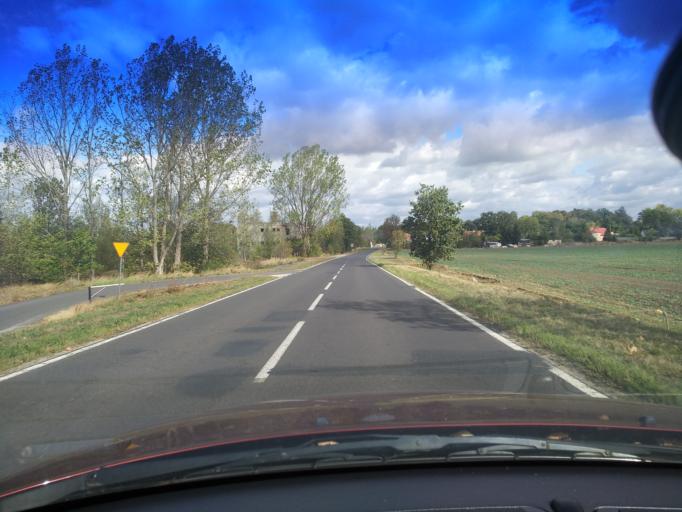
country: PL
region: Lower Silesian Voivodeship
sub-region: Powiat zgorzelecki
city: Zgorzelec
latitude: 51.1805
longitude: 15.0134
